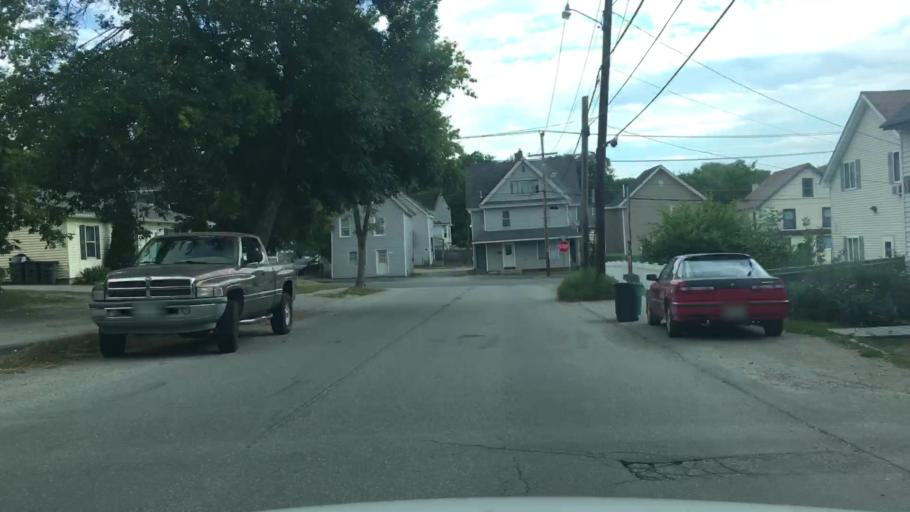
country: US
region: Maine
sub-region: Penobscot County
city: Bangor
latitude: 44.8098
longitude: -68.7729
